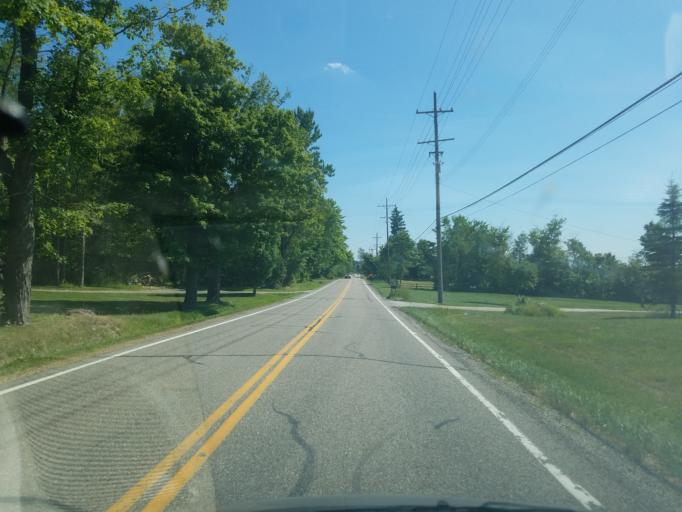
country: US
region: Ohio
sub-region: Geauga County
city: Burton
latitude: 41.5133
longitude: -81.1442
